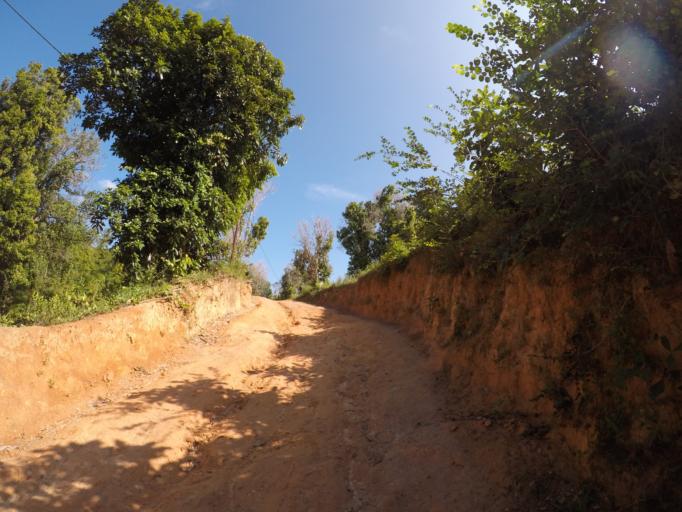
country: TZ
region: Pemba South
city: Mtambile
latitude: -5.3844
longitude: 39.7215
